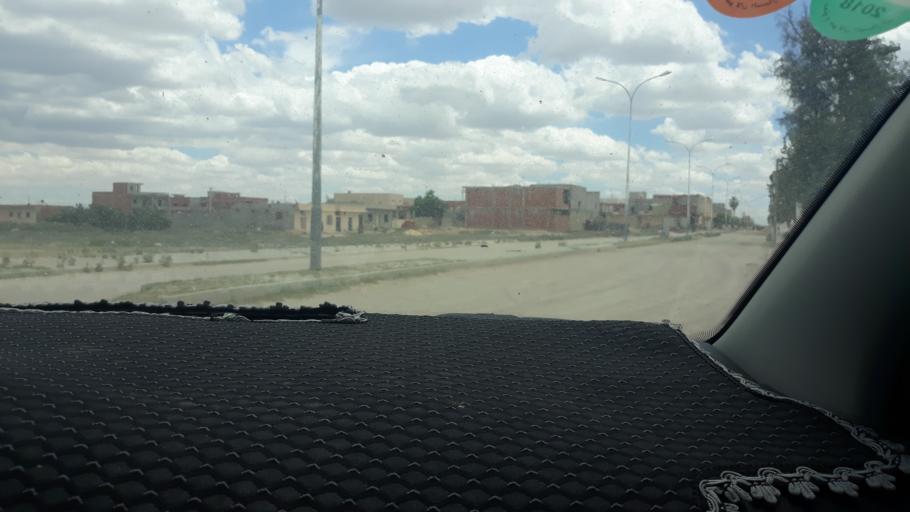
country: TN
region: Al Qayrawan
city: Kairouan
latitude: 35.6239
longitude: 9.9242
